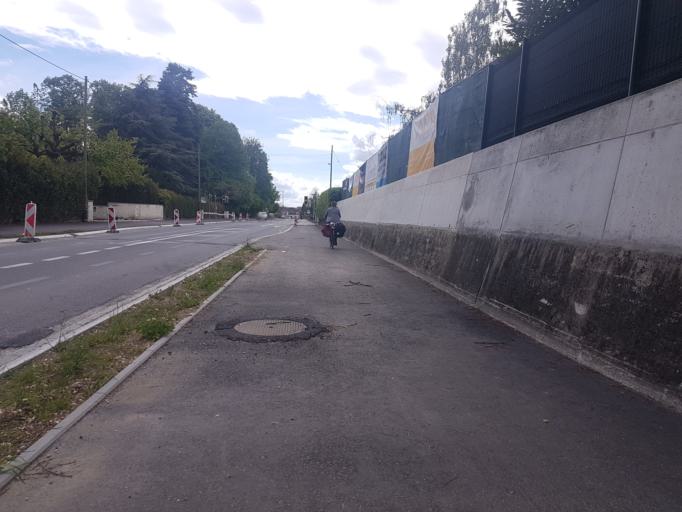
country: CH
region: Vaud
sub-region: Nyon District
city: Coppet
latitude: 46.3219
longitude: 6.1966
